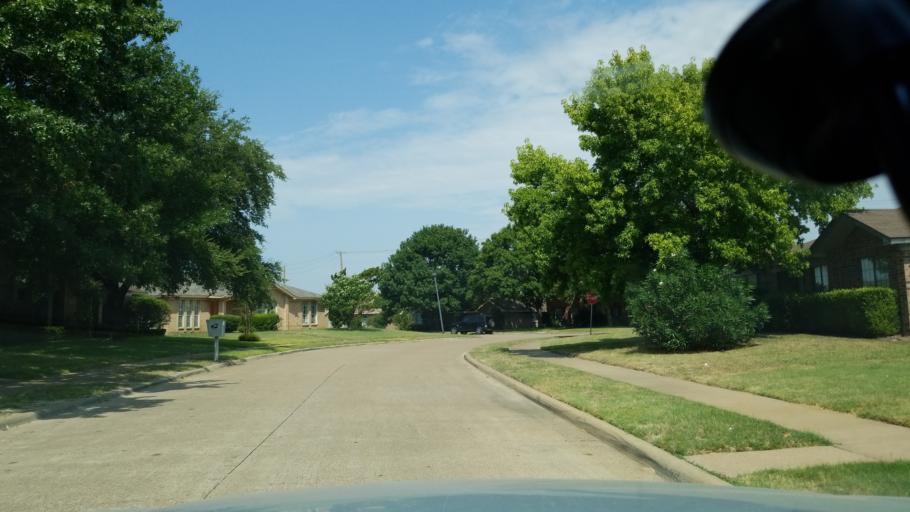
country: US
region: Texas
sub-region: Dallas County
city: Cockrell Hill
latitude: 32.6892
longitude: -96.8448
